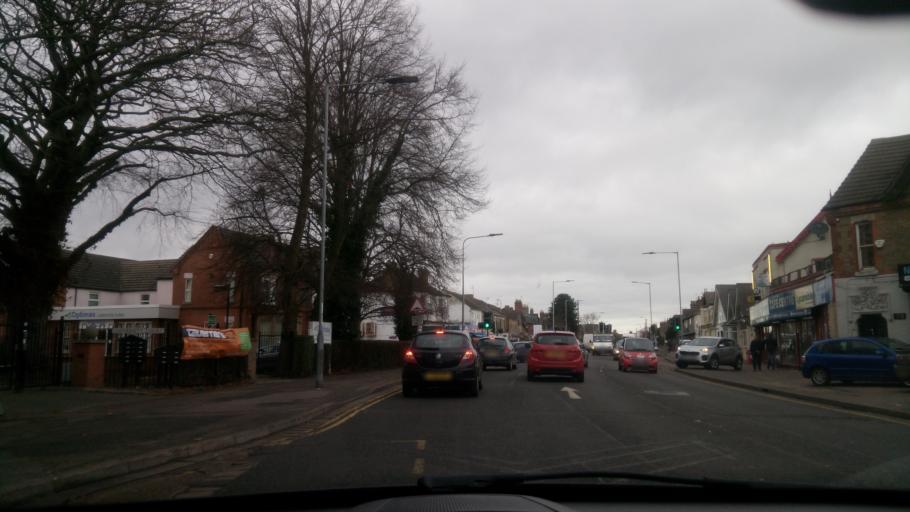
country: GB
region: England
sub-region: Peterborough
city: Peterborough
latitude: 52.5834
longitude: -0.2452
